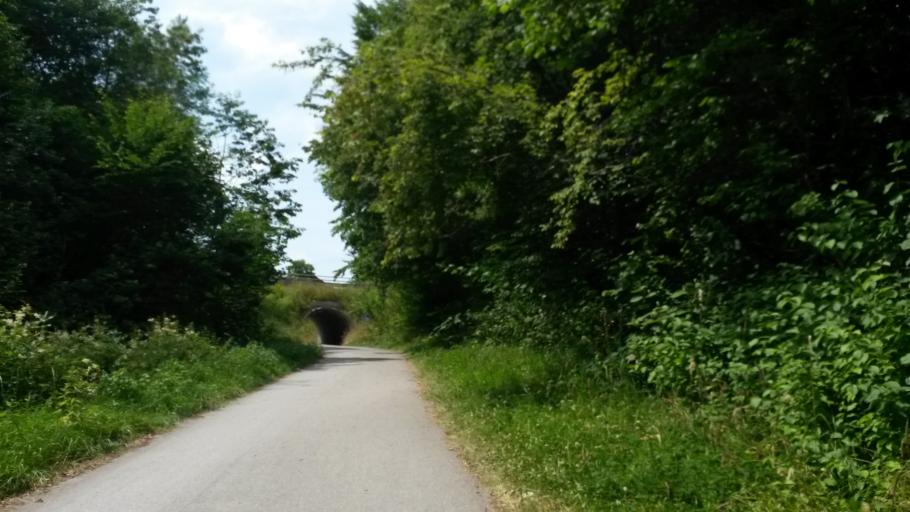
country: DE
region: Bavaria
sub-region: Upper Bavaria
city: Gstadt am Chiemsee
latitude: 47.9041
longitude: 12.4311
